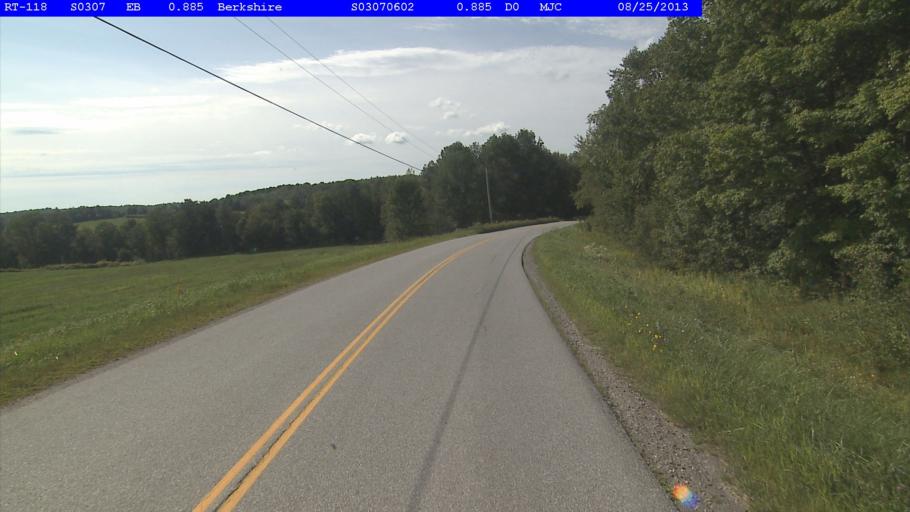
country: US
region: Vermont
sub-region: Franklin County
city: Enosburg Falls
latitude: 44.9358
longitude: -72.7290
